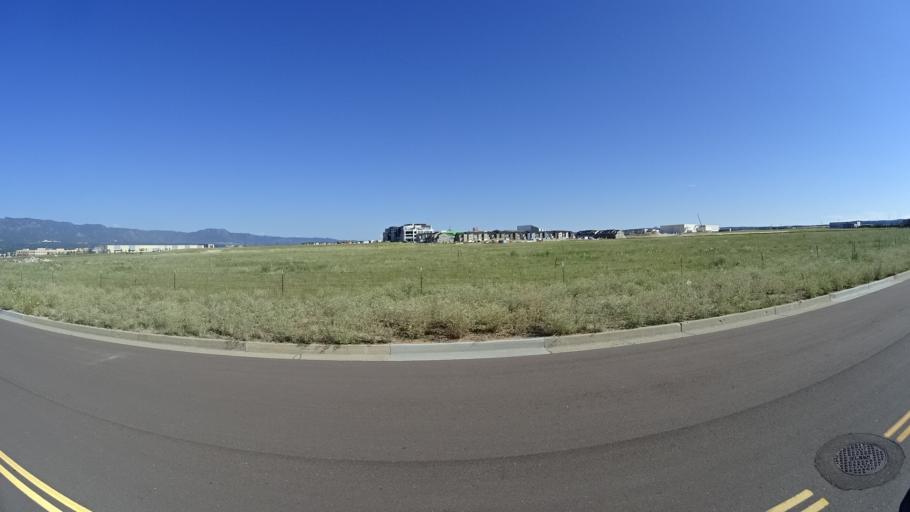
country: US
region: Colorado
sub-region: El Paso County
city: Gleneagle
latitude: 38.9822
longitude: -104.7926
